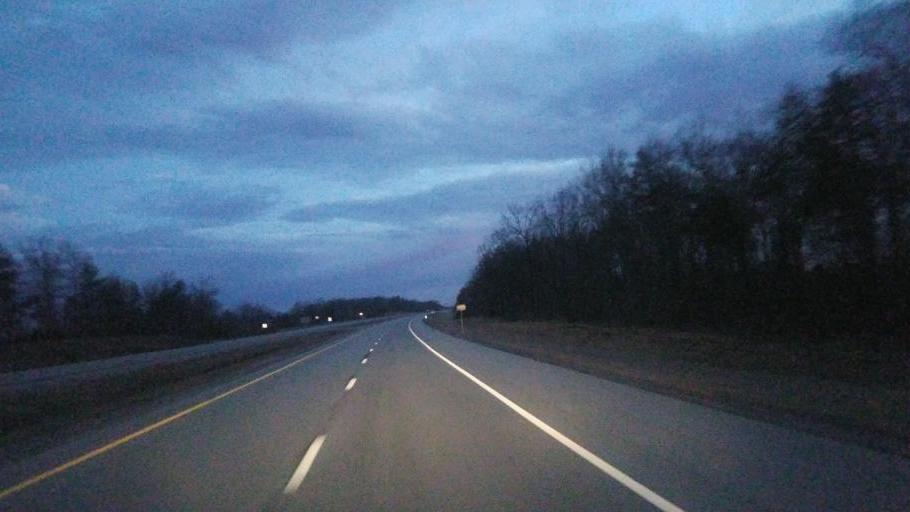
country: US
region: Tennessee
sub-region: Van Buren County
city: Spencer
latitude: 35.5541
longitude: -85.4707
